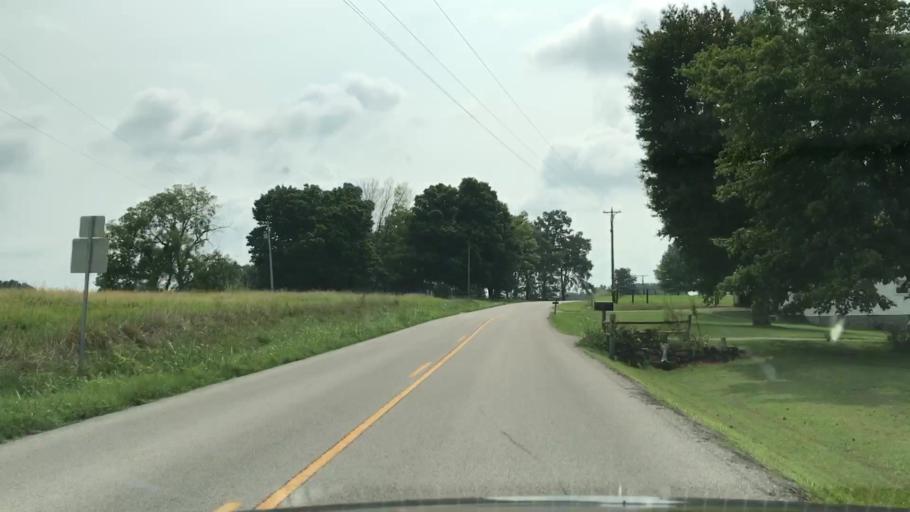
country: US
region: Kentucky
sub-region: Edmonson County
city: Brownsville
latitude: 37.1408
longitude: -86.1824
